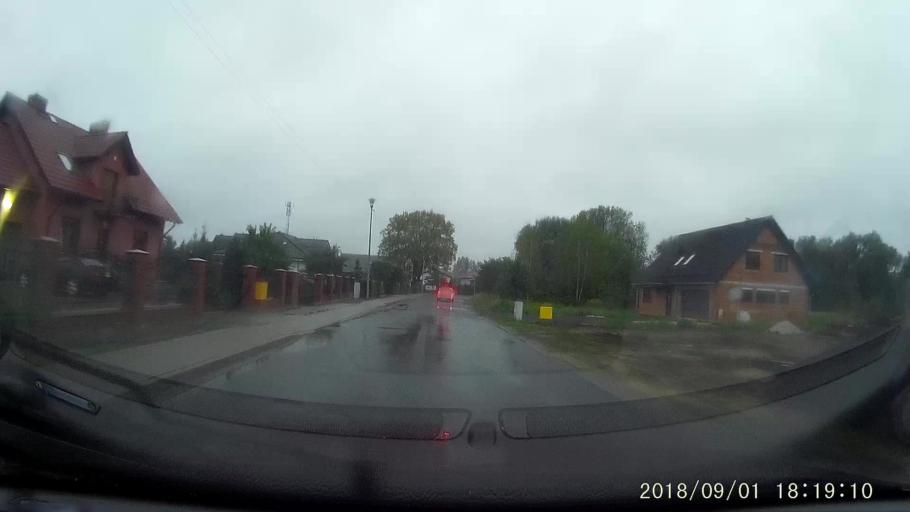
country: PL
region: Lower Silesian Voivodeship
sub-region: Powiat zgorzelecki
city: Piensk
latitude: 51.2561
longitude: 15.0460
